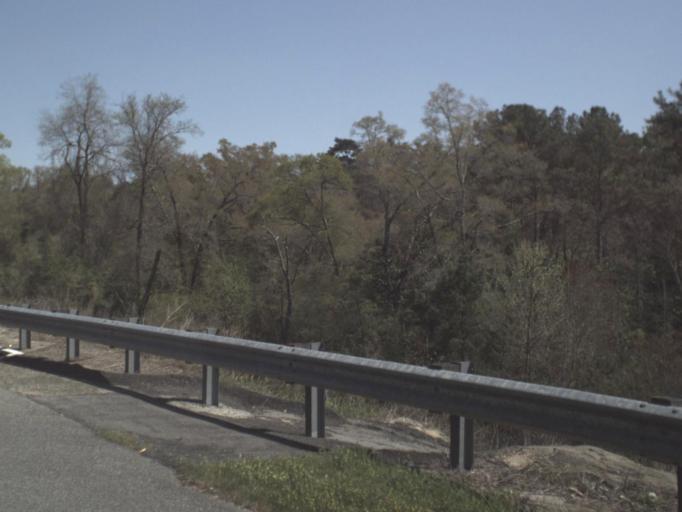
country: US
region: Florida
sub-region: Liberty County
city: Bristol
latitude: 30.4315
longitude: -84.9873
